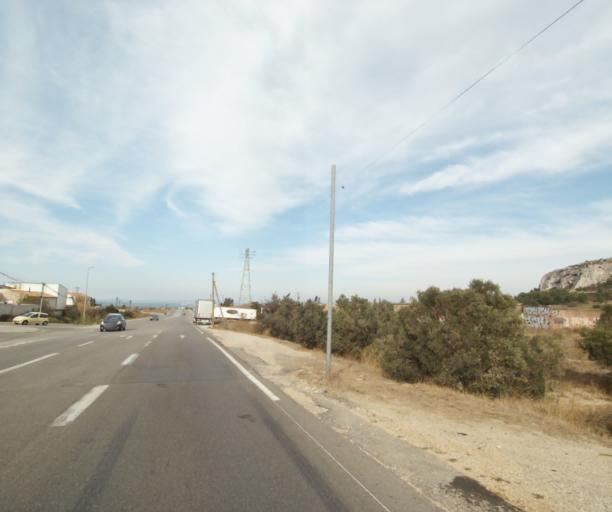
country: FR
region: Provence-Alpes-Cote d'Azur
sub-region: Departement des Bouches-du-Rhone
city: Gignac-la-Nerthe
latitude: 43.3764
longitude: 5.2270
